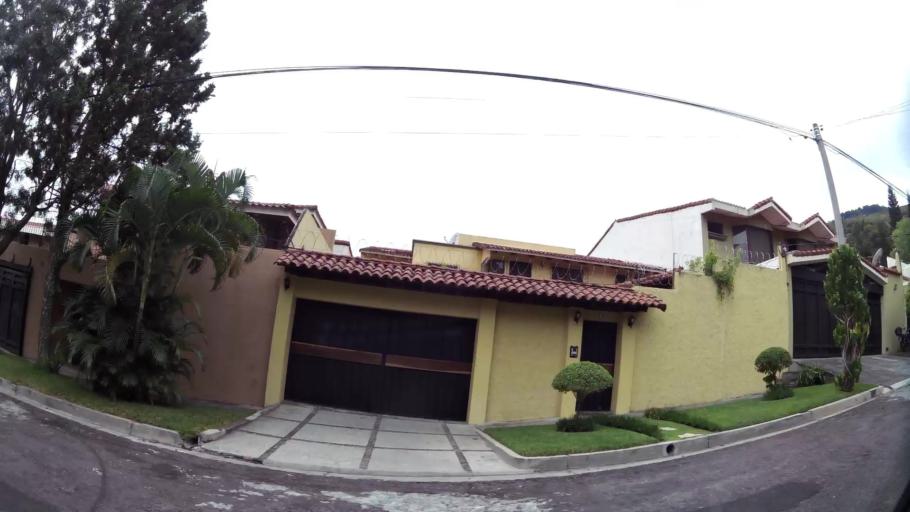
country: SV
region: San Salvador
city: Mejicanos
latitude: 13.7196
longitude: -89.2460
